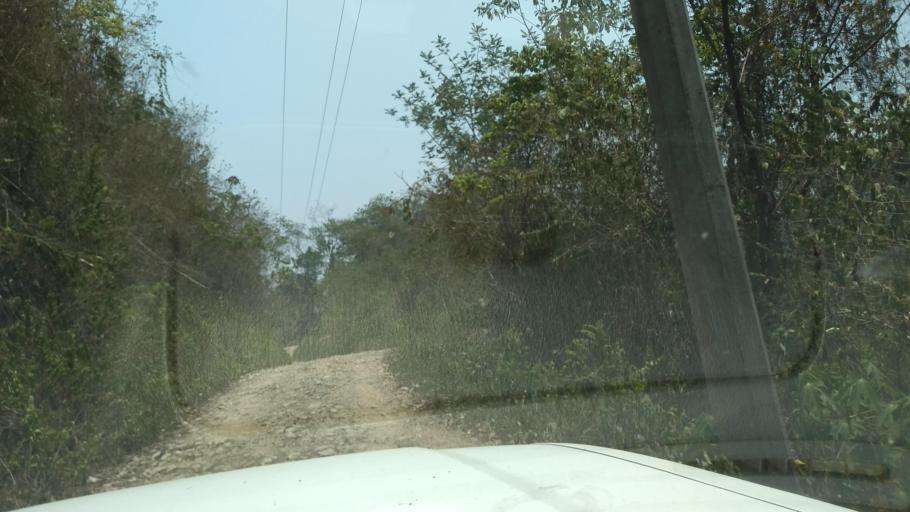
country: MX
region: Veracruz
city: Motzorongo
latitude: 18.5958
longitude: -96.7325
